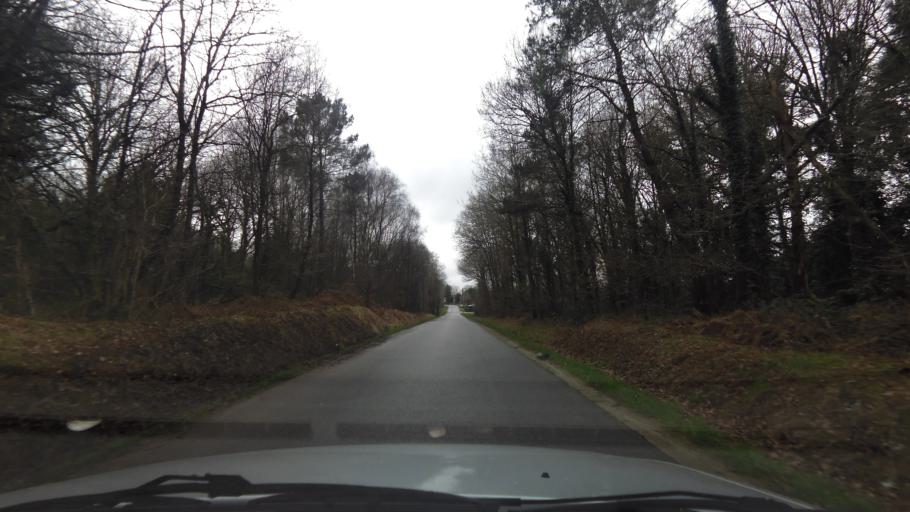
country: FR
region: Brittany
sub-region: Departement du Morbihan
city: Serent
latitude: 47.7823
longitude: -2.5498
